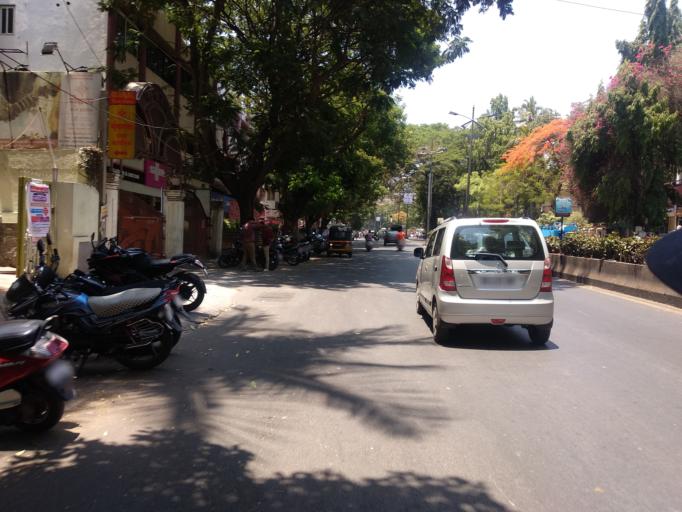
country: IN
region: Maharashtra
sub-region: Pune Division
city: Pune
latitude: 18.5082
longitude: 73.8442
